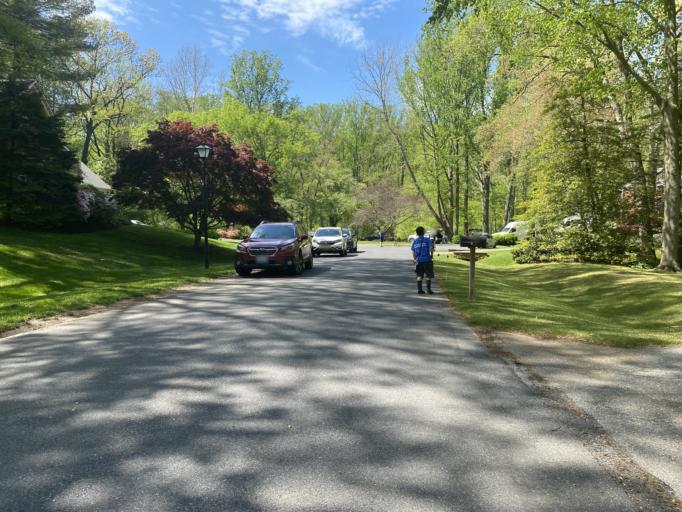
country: US
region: Maryland
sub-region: Montgomery County
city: Potomac
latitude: 39.0525
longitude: -77.2052
